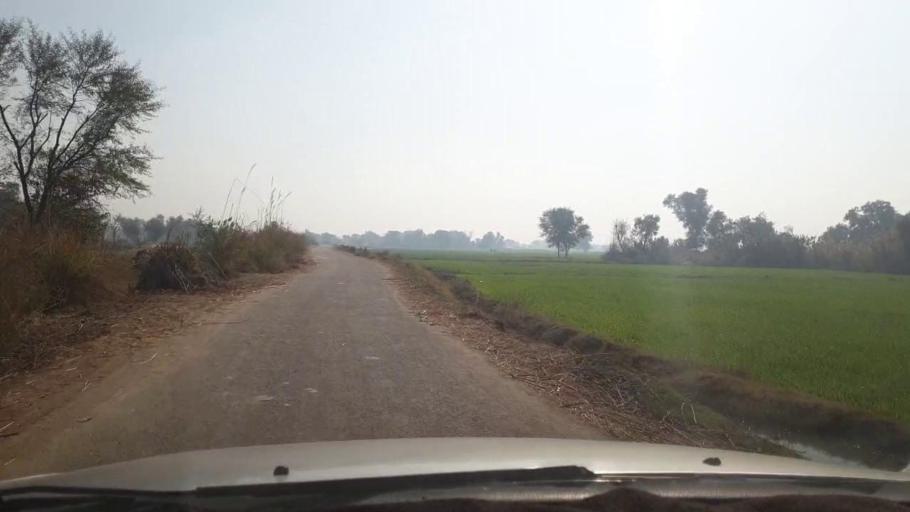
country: PK
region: Sindh
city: Khanpur
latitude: 27.7330
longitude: 69.5125
